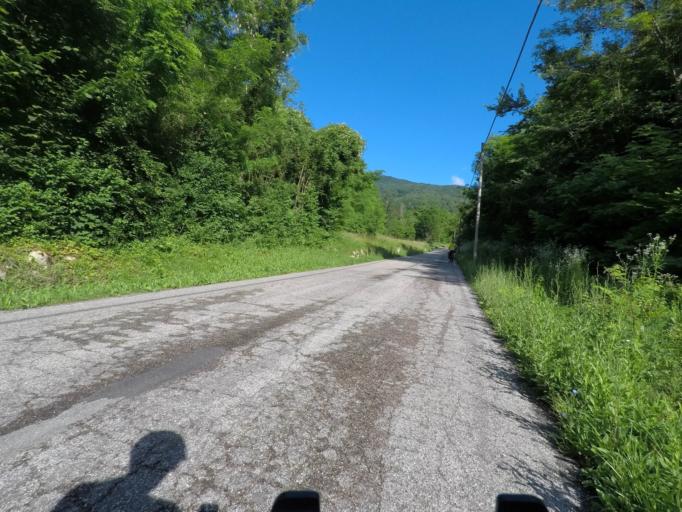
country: IT
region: Friuli Venezia Giulia
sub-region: Provincia di Udine
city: Pulfero
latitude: 46.1566
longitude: 13.4815
